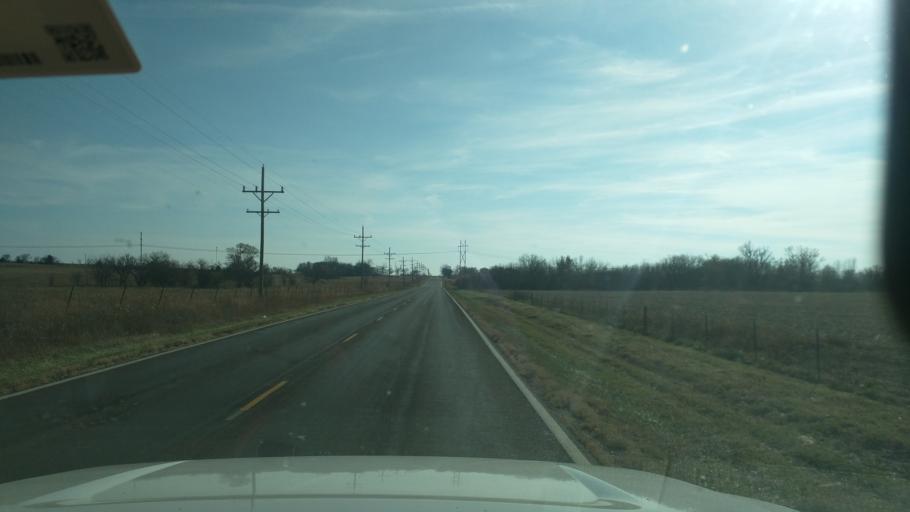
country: US
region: Kansas
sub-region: Lyon County
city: Emporia
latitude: 38.2941
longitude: -96.1805
